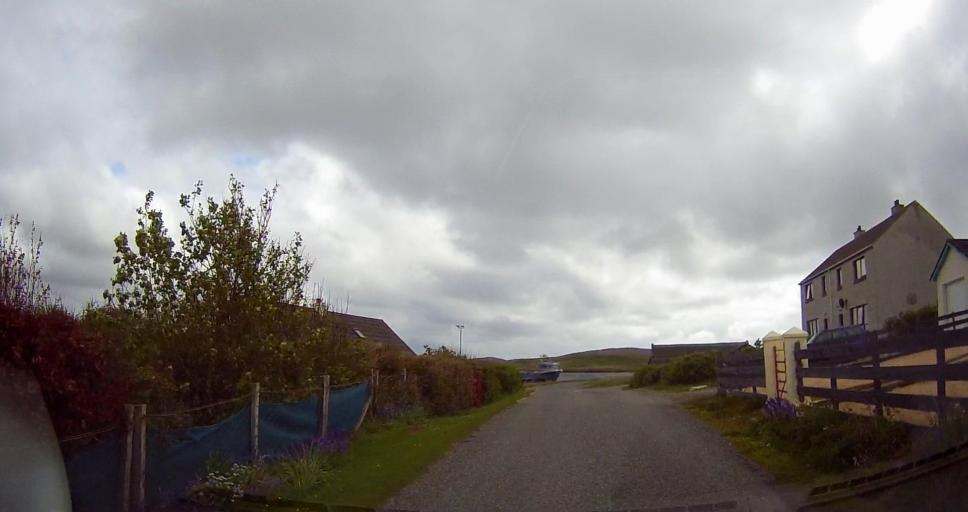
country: GB
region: Scotland
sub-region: Shetland Islands
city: Sandwick
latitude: 60.2245
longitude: -1.5700
